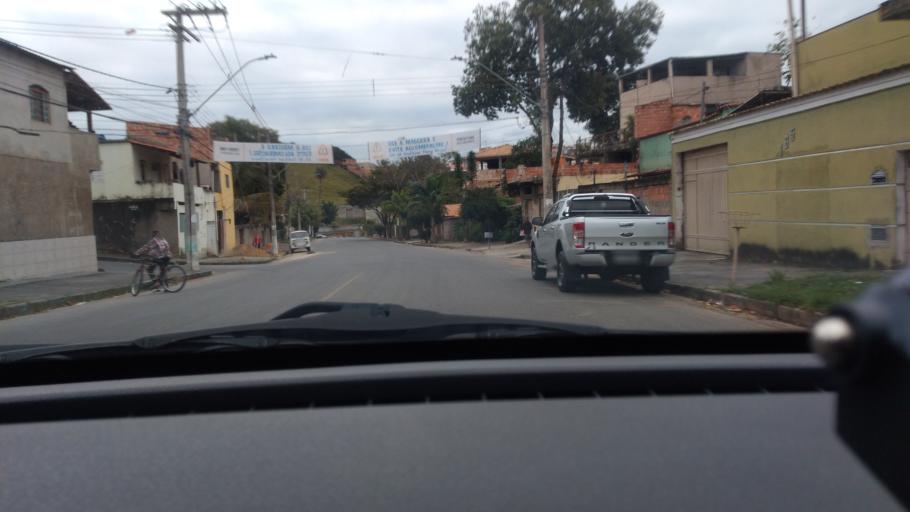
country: BR
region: Minas Gerais
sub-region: Belo Horizonte
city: Belo Horizonte
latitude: -19.8234
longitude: -43.9354
